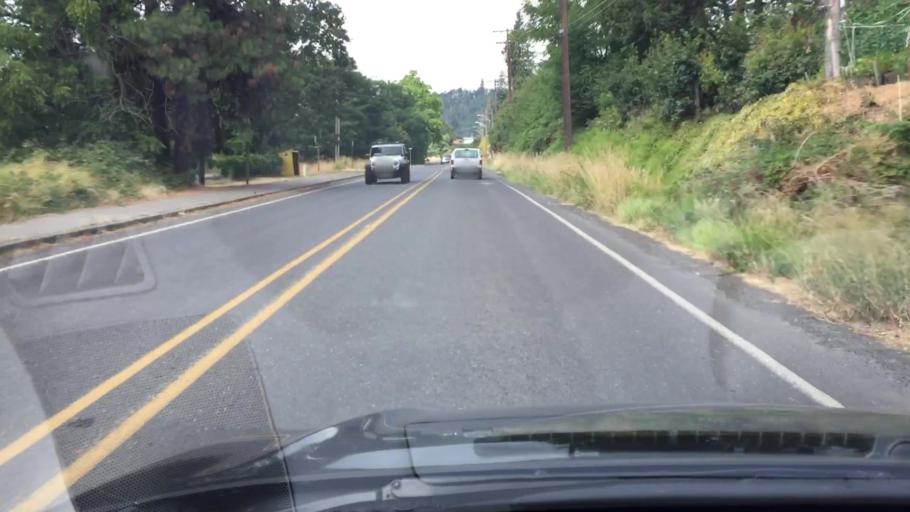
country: US
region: Washington
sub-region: Klickitat County
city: White Salmon
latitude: 45.7243
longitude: -121.4767
